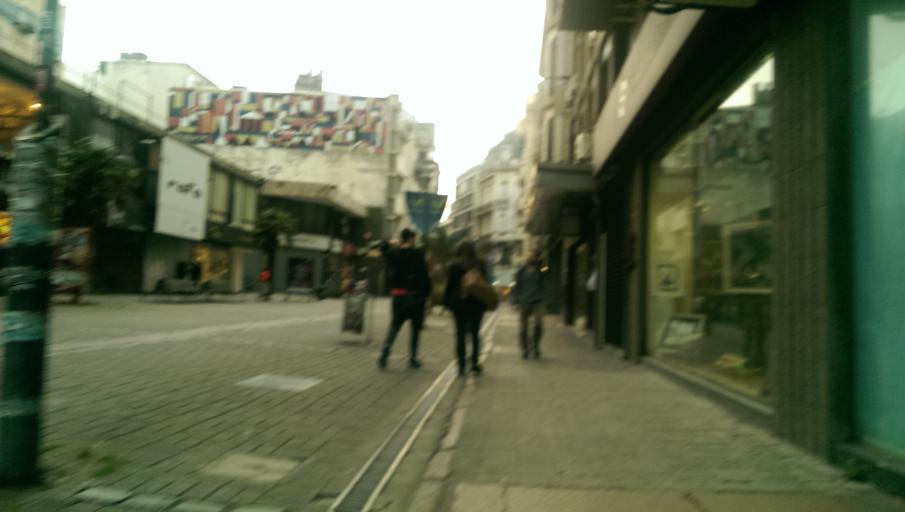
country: UY
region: Montevideo
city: Montevideo
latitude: -34.9065
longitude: -56.2010
